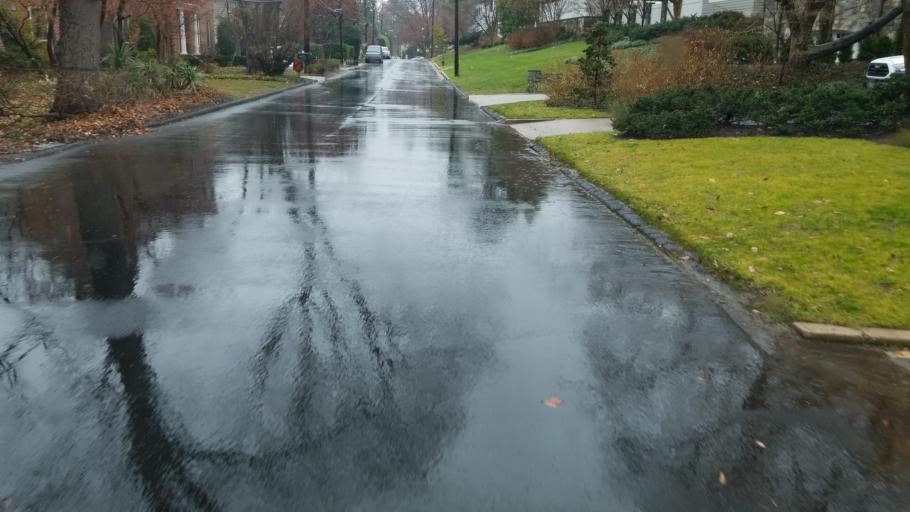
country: US
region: Maryland
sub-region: Montgomery County
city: Brookmont
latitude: 38.9304
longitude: -77.0973
